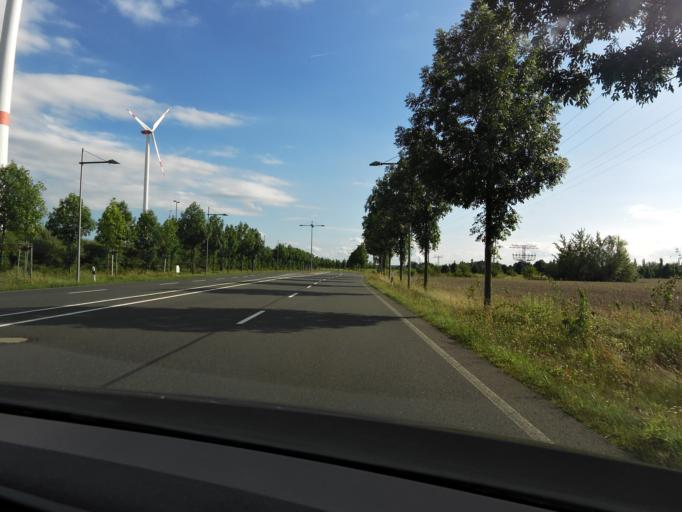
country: DE
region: Saxony
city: Taucha
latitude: 51.4047
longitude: 12.4321
